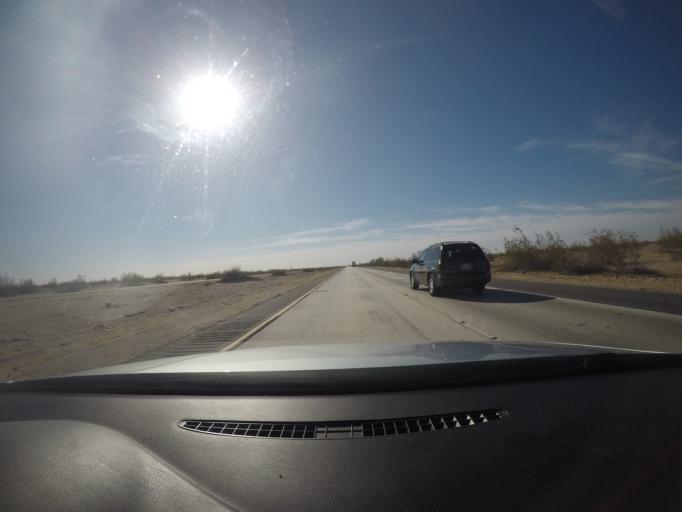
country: US
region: California
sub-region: Imperial County
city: Holtville
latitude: 32.7503
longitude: -115.2164
